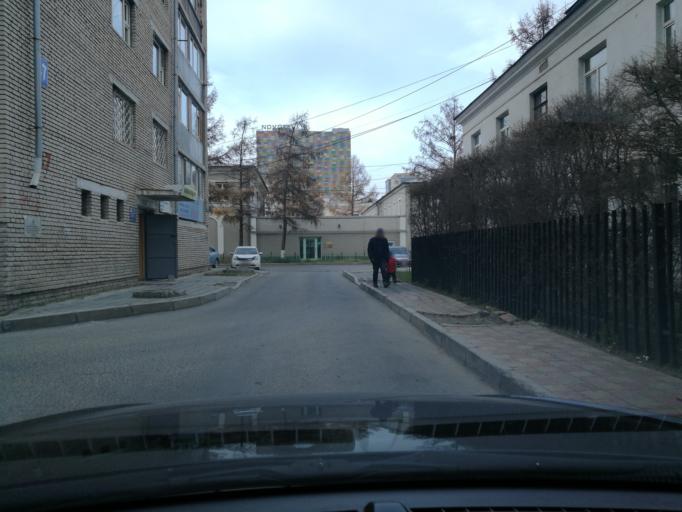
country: MN
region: Ulaanbaatar
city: Ulaanbaatar
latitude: 47.9241
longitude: 106.9177
